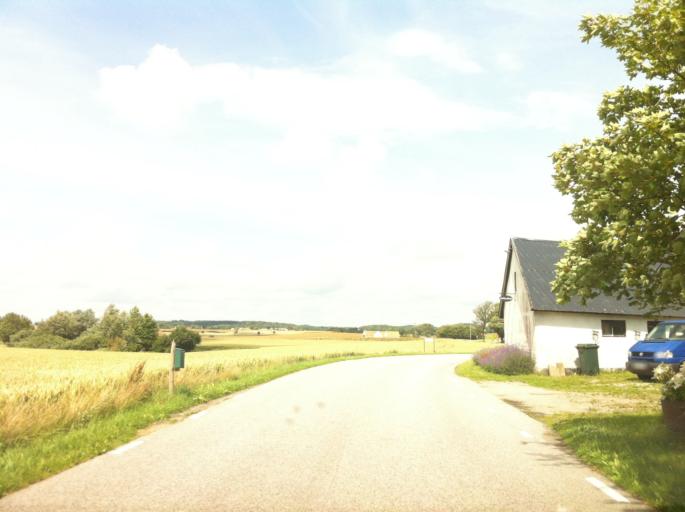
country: SE
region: Skane
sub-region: Skurups Kommun
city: Skurup
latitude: 55.4587
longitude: 13.4290
